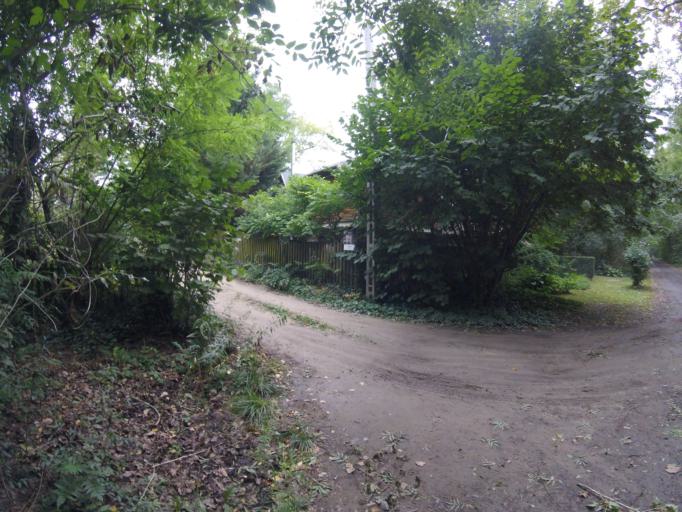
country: HU
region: Pest
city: Szentendre
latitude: 47.6632
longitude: 19.1052
